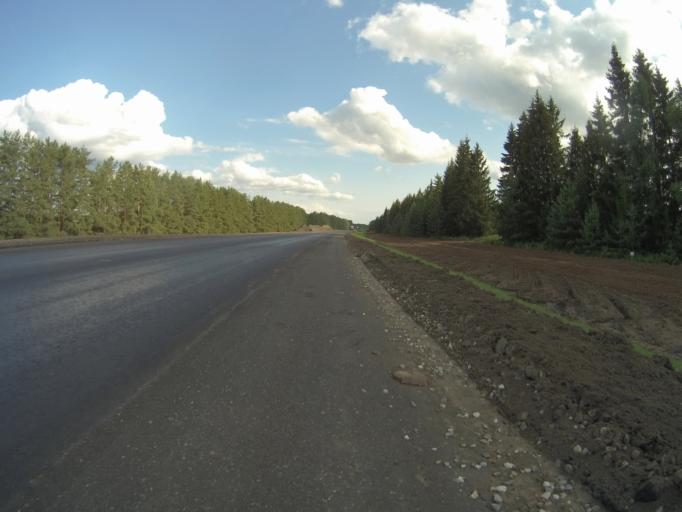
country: RU
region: Vladimir
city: Kideksha
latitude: 56.5439
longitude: 40.5539
